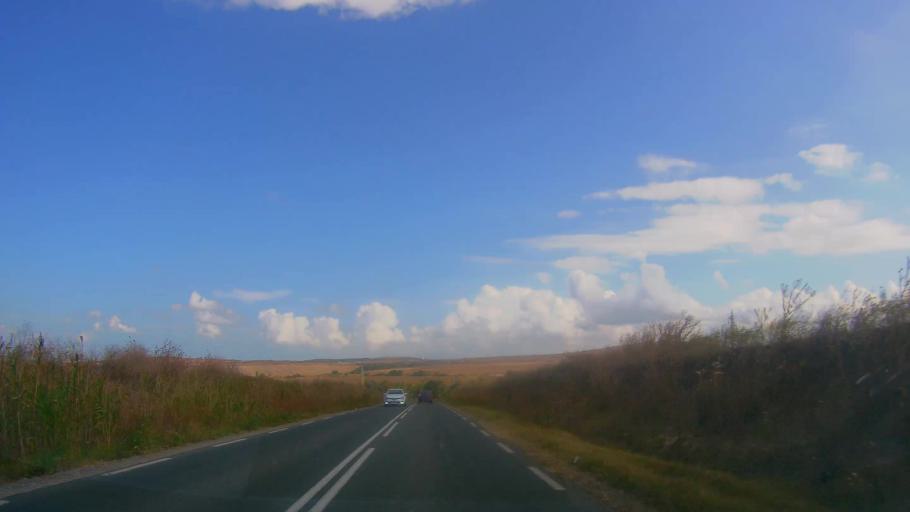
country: BG
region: Burgas
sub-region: Obshtina Kameno
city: Kameno
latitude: 42.4776
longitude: 27.3524
